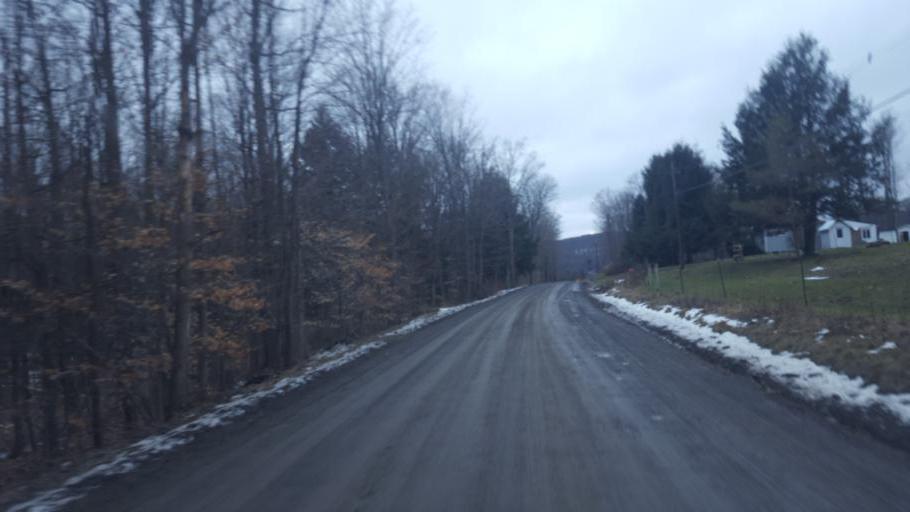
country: US
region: New York
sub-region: Allegany County
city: Andover
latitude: 41.9301
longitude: -77.7781
